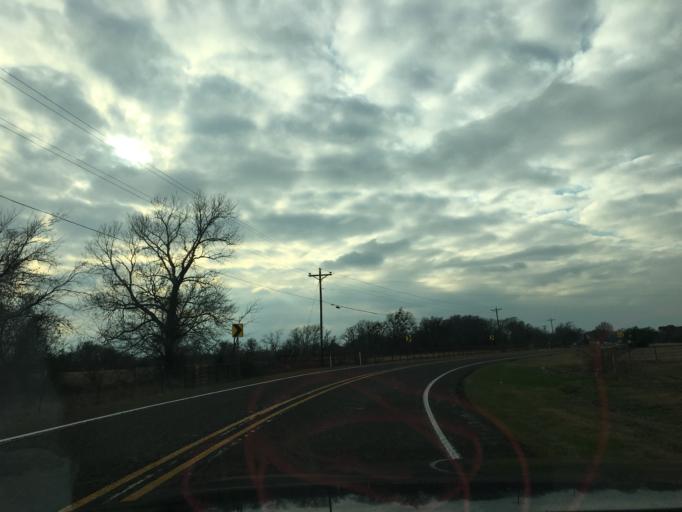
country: US
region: Texas
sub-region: Ellis County
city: Palmer
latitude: 32.4483
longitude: -96.7111
